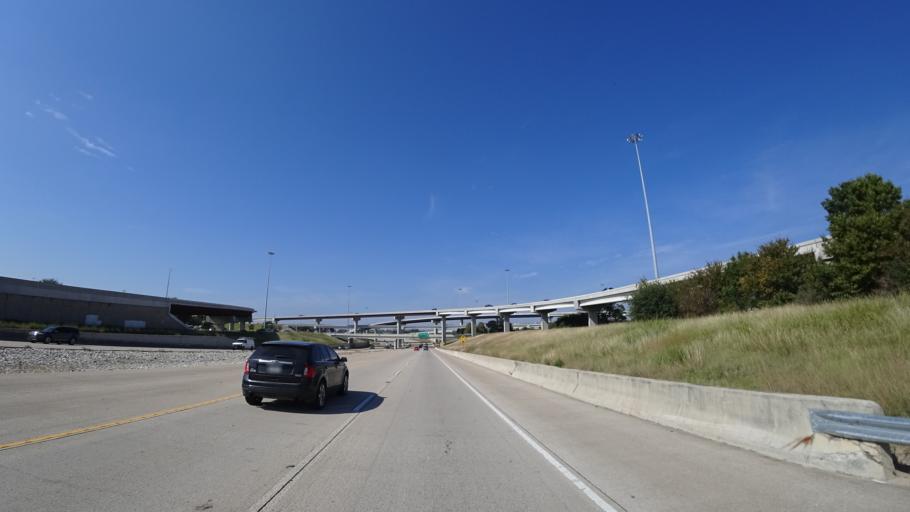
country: US
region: Texas
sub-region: Travis County
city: Rollingwood
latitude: 30.2341
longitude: -97.8215
